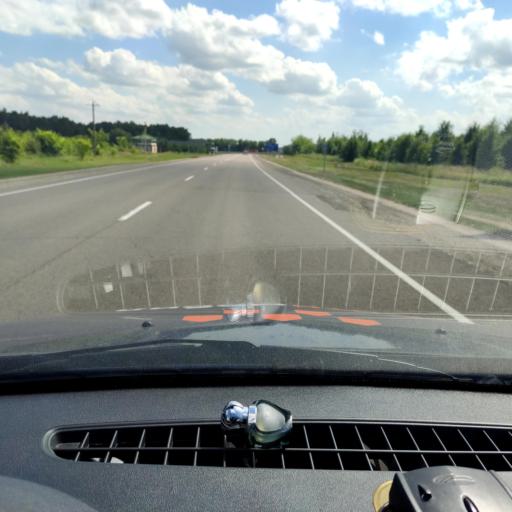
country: RU
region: Orjol
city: Livny
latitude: 52.4251
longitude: 37.6486
